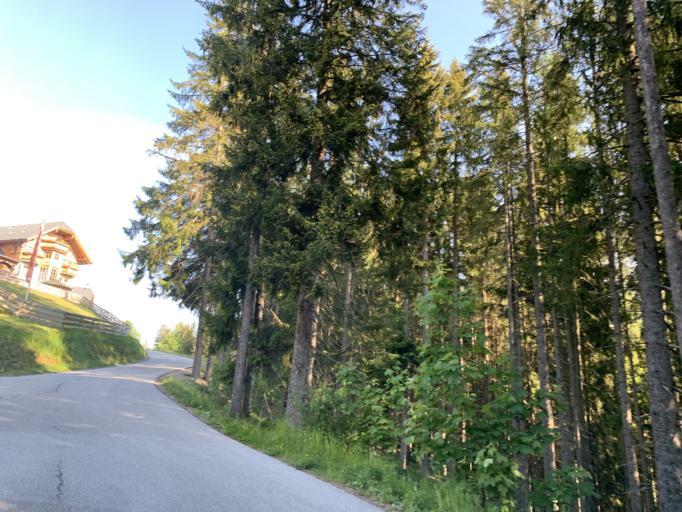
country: AT
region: Salzburg
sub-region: Politischer Bezirk Sankt Johann im Pongau
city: Forstau
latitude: 47.3765
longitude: 13.6089
